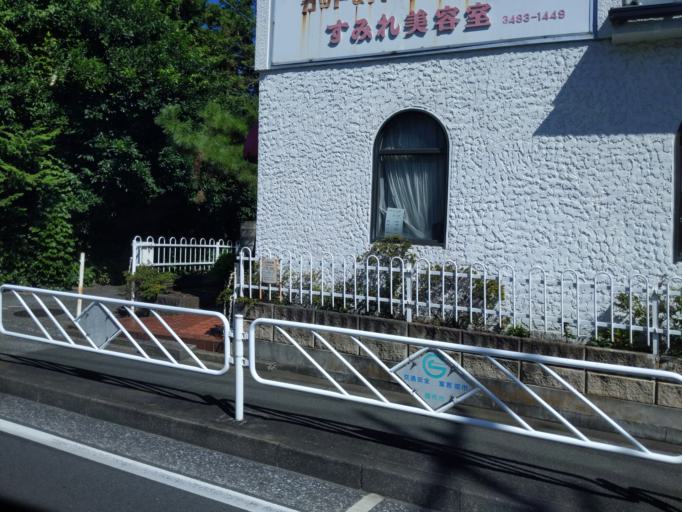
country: JP
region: Tokyo
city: Chofugaoka
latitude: 35.6496
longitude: 139.5918
